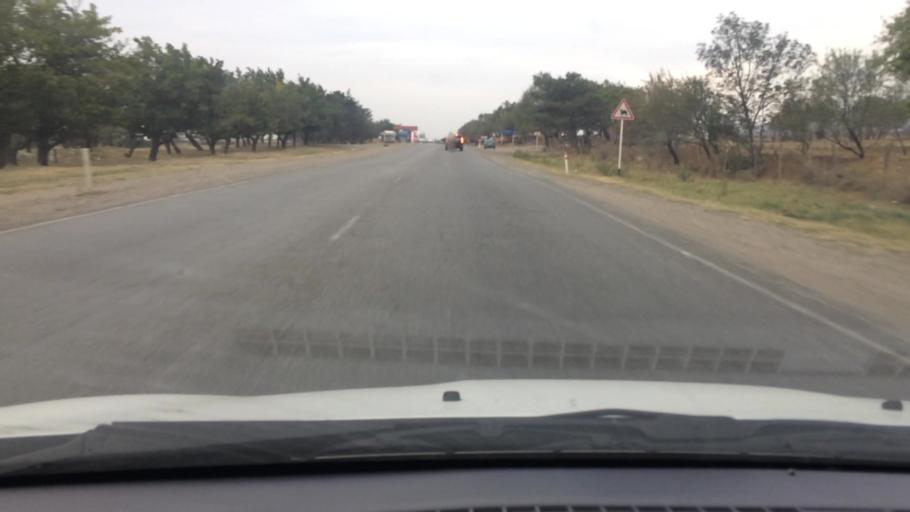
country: GE
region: T'bilisi
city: Tbilisi
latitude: 41.6358
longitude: 44.8231
